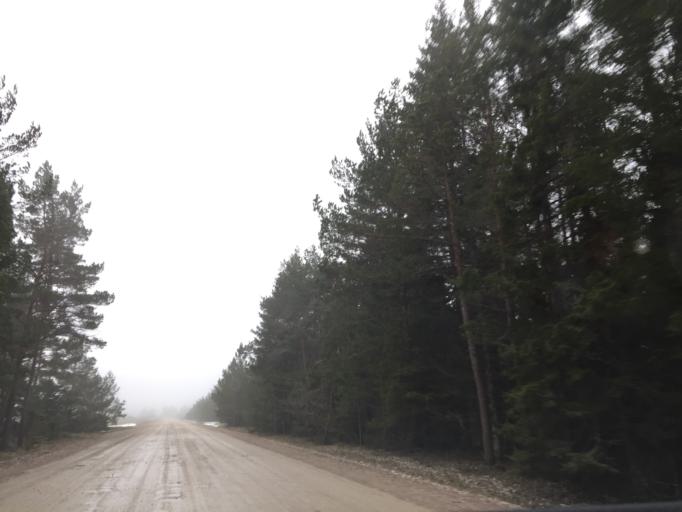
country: EE
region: Saare
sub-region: Kuressaare linn
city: Kuressaare
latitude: 58.4714
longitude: 22.0019
